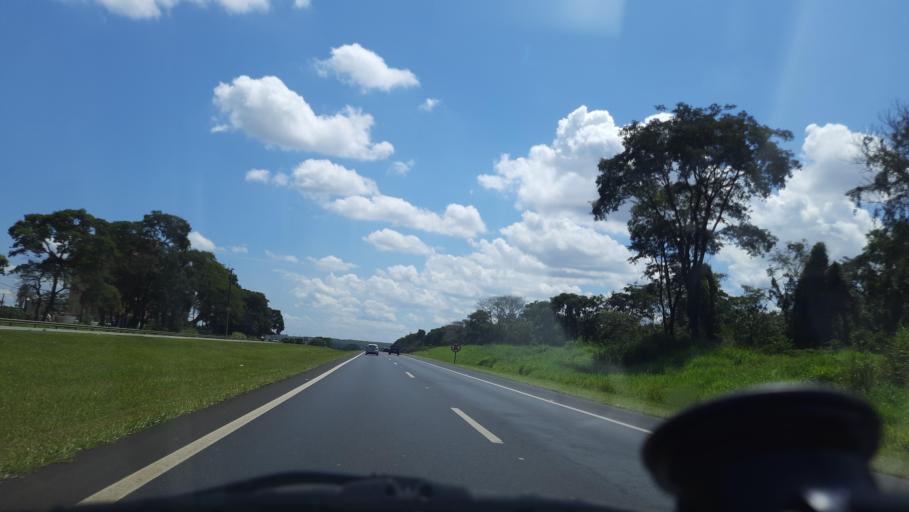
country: BR
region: Sao Paulo
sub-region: Moji-Guacu
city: Mogi-Gaucu
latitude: -22.3805
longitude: -46.9711
